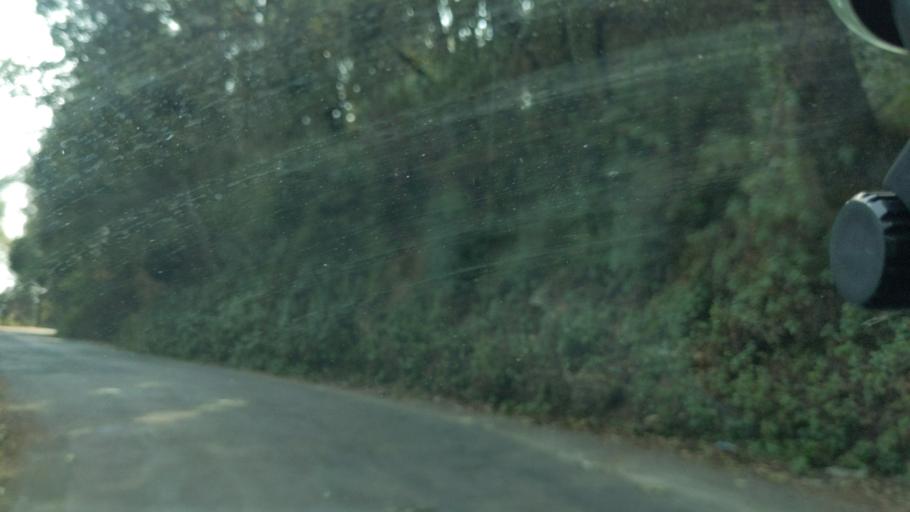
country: IN
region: Uttarakhand
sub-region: Naini Tal
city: Bhowali
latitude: 29.4071
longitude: 79.5395
